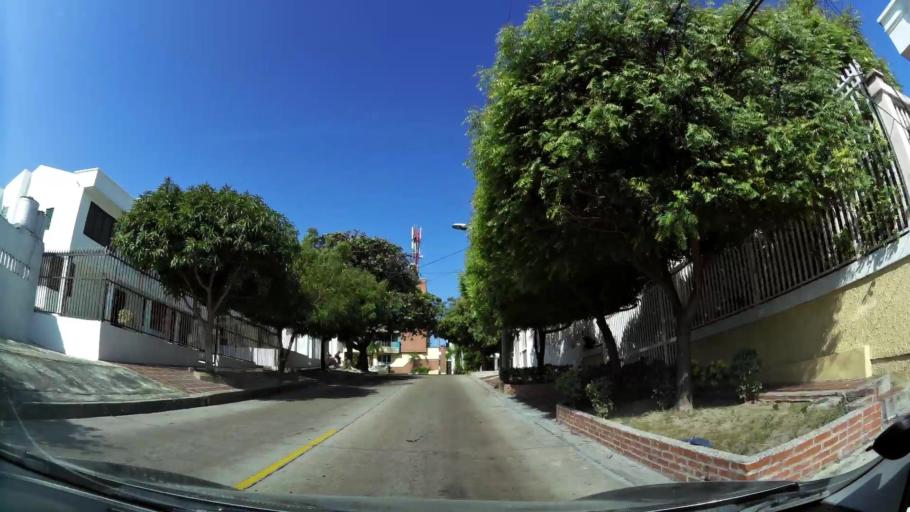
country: CO
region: Atlantico
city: Barranquilla
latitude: 10.9914
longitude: -74.8229
